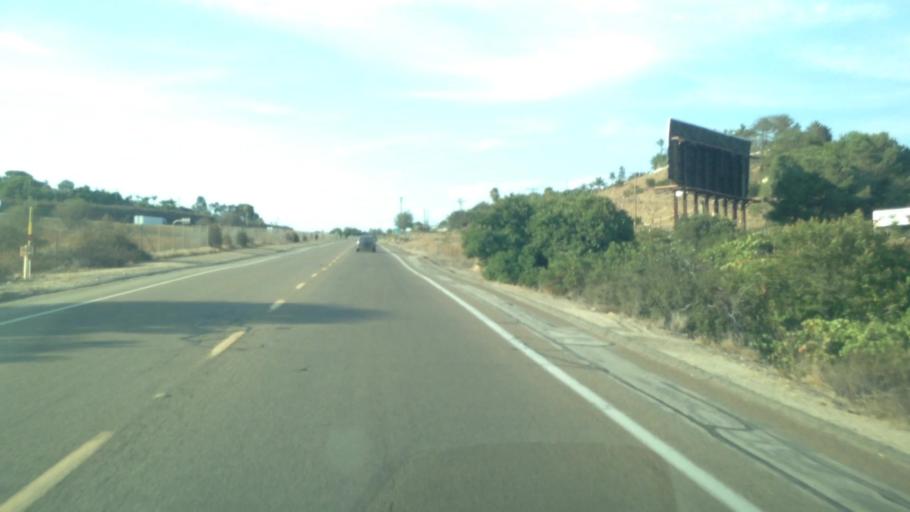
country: US
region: California
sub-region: San Diego County
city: Rainbow
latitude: 33.3943
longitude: -117.1719
